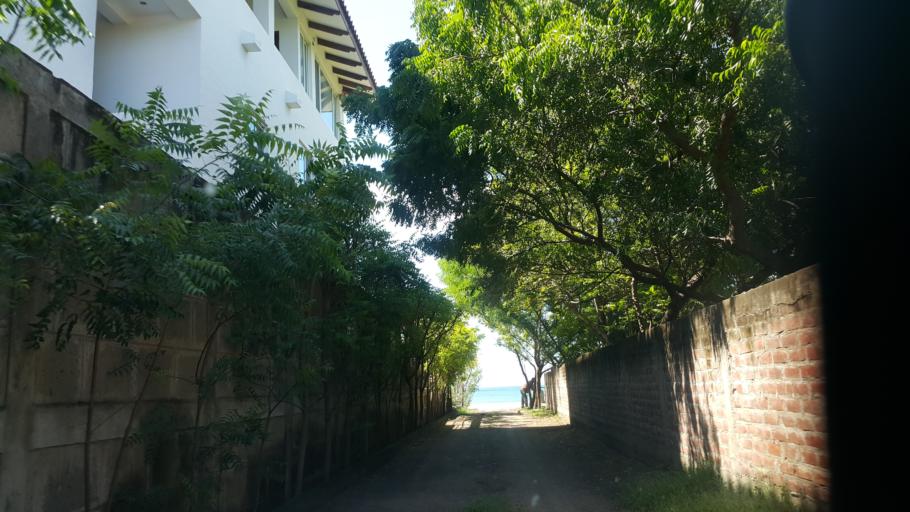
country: NI
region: Rivas
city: San Juan del Sur
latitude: 11.2857
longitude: -85.9024
